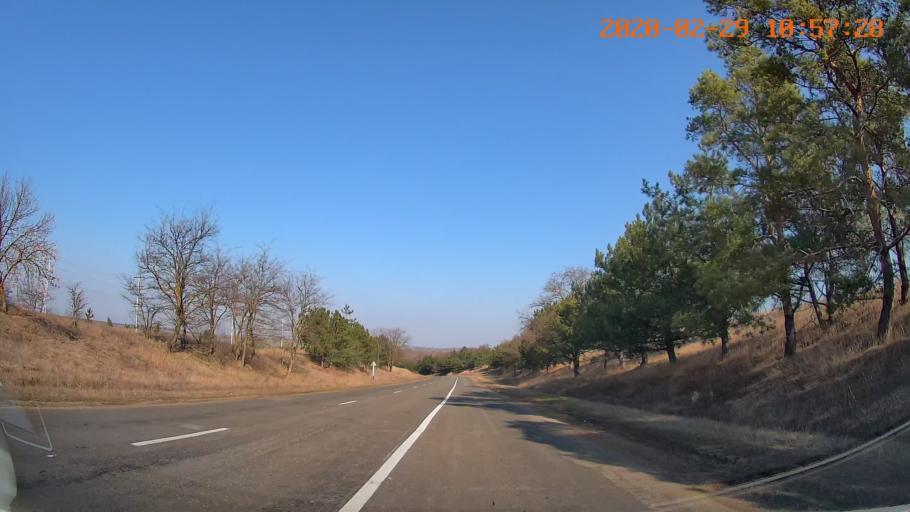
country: MD
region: Telenesti
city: Grigoriopol
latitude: 47.1596
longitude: 29.3219
